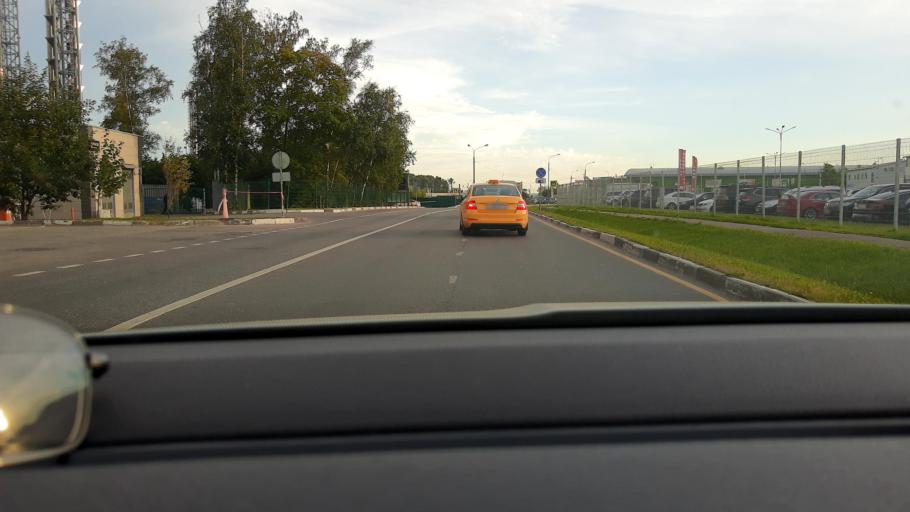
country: RU
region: Moskovskaya
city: Opalikha
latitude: 55.7852
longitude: 37.2395
